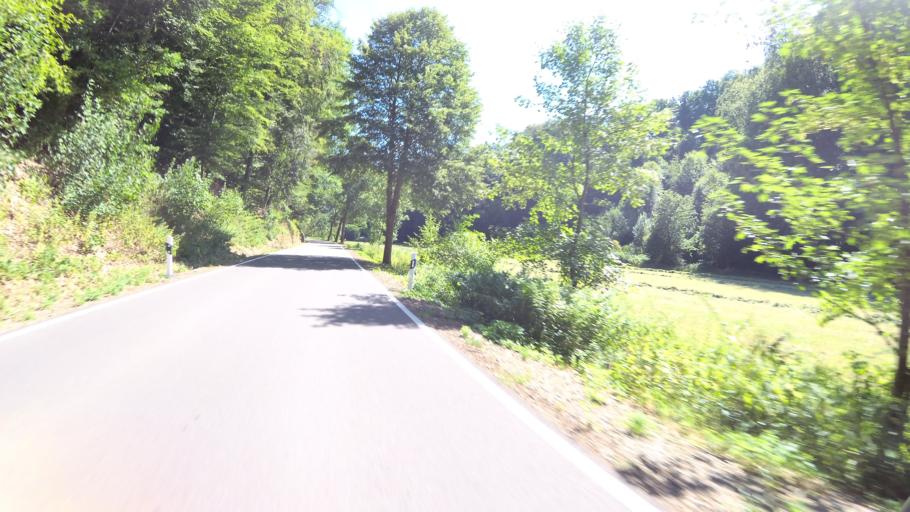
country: DE
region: Rheinland-Pfalz
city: Zweibrucken
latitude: 49.2515
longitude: 7.3127
